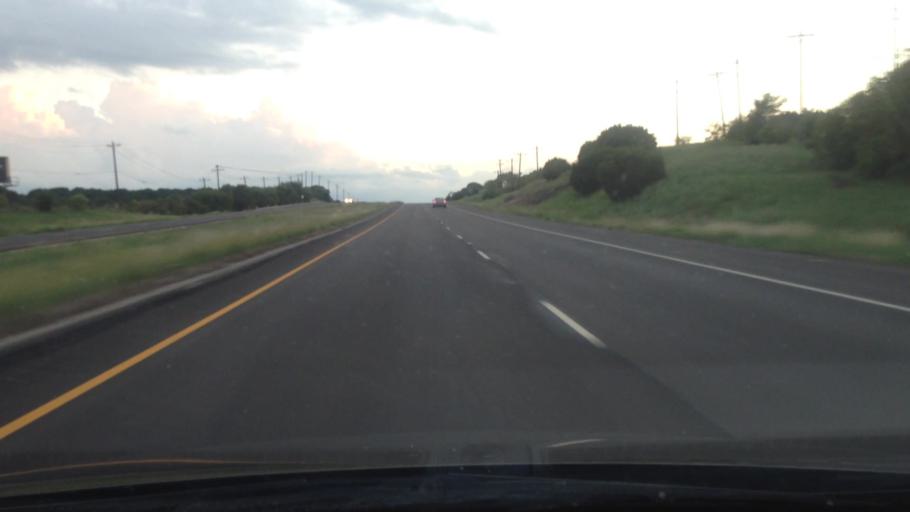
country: US
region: Texas
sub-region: Hood County
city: DeCordova
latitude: 32.5196
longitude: -97.6284
